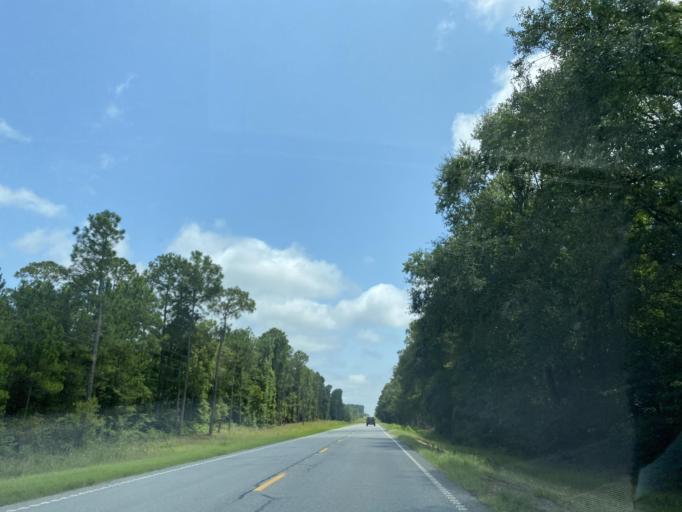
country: US
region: Georgia
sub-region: Telfair County
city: McRae
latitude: 32.1000
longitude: -82.8437
